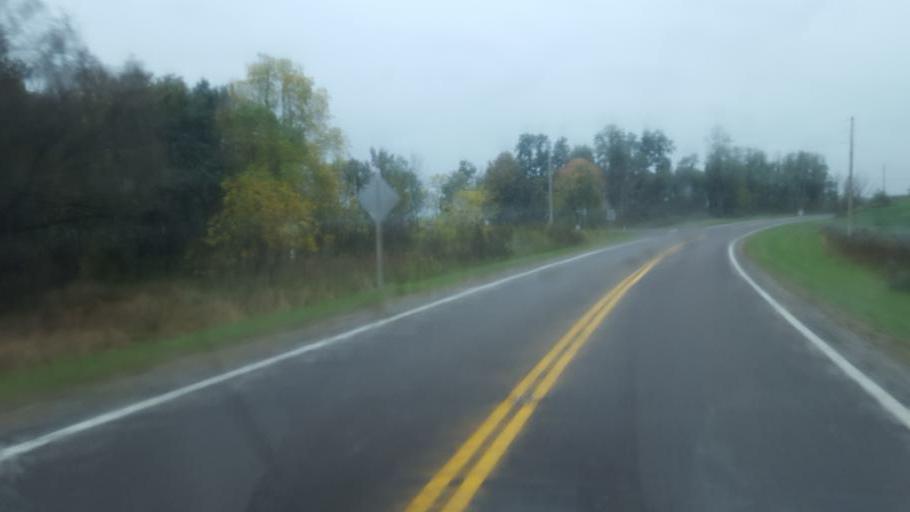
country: US
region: Ohio
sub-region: Richland County
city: Lincoln Heights
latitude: 40.8645
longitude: -82.4398
